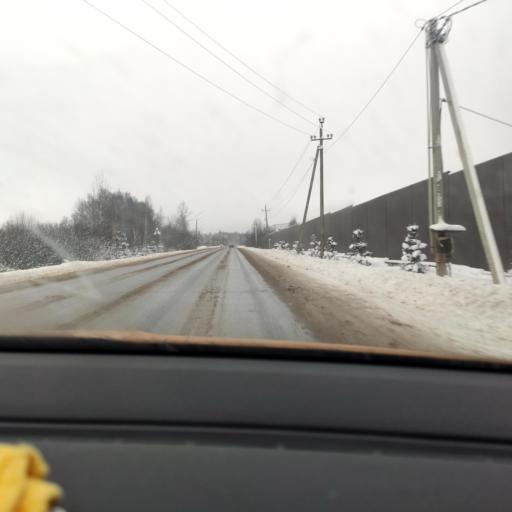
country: RU
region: Moskovskaya
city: Yershovo
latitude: 55.7562
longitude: 36.8694
